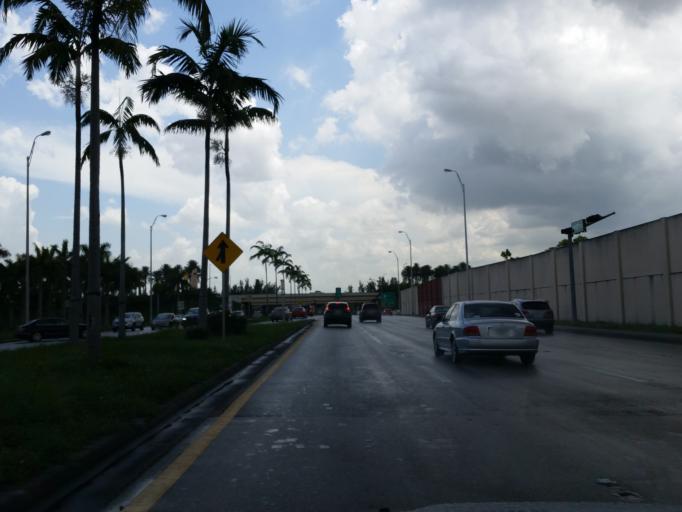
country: US
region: Florida
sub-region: Miami-Dade County
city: Sweetwater
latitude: 25.7777
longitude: -80.3693
